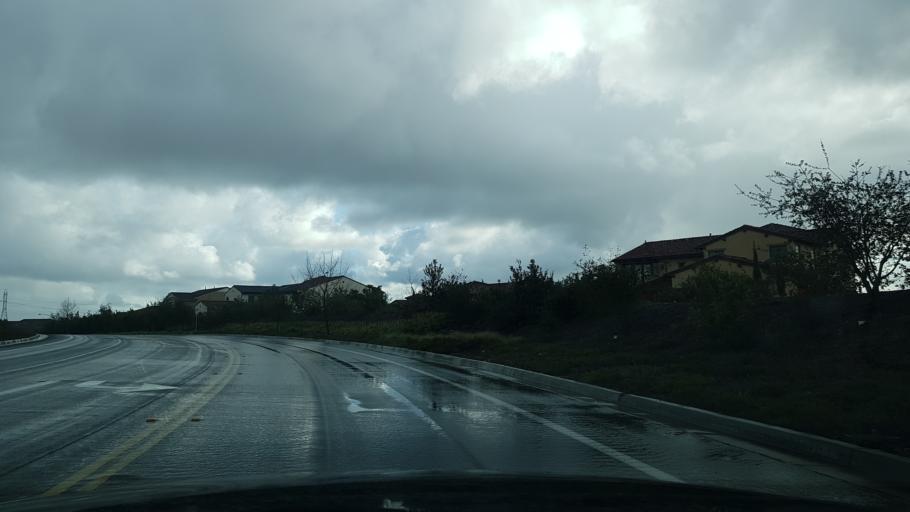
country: US
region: California
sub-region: San Diego County
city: Fairbanks Ranch
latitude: 32.9381
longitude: -117.1830
